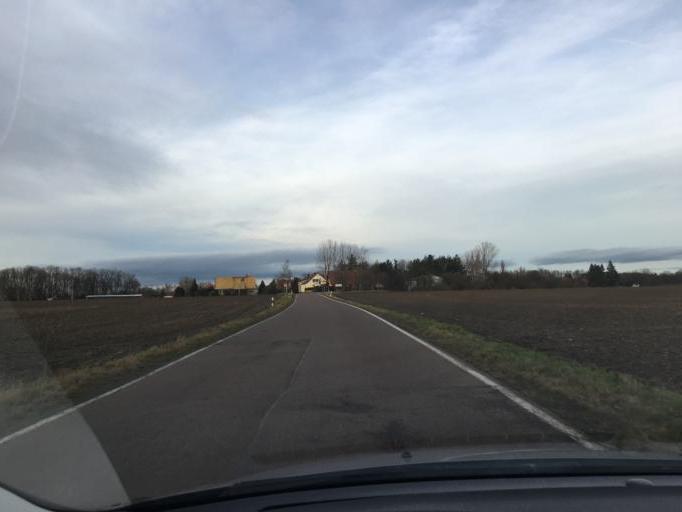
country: DE
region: Saxony
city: Grossposna
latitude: 51.2382
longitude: 12.4843
